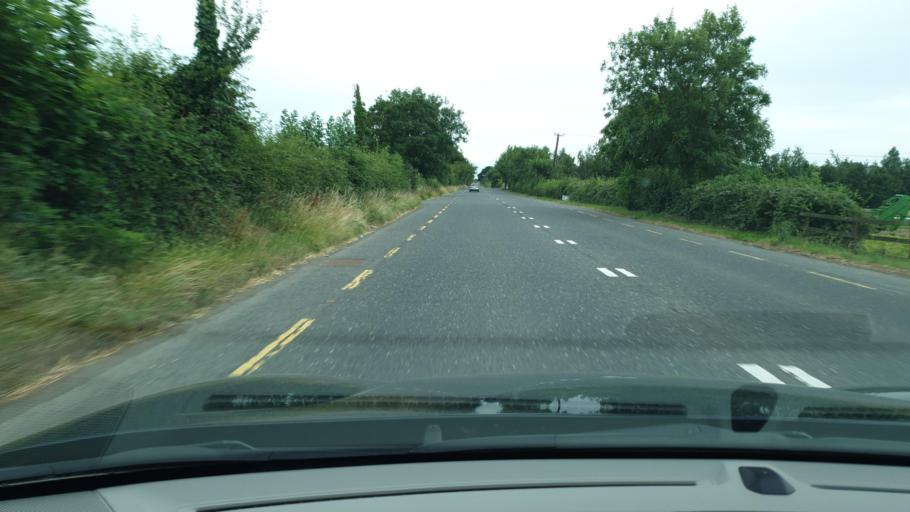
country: IE
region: Leinster
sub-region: An Mhi
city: Ashbourne
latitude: 53.4915
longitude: -6.3799
